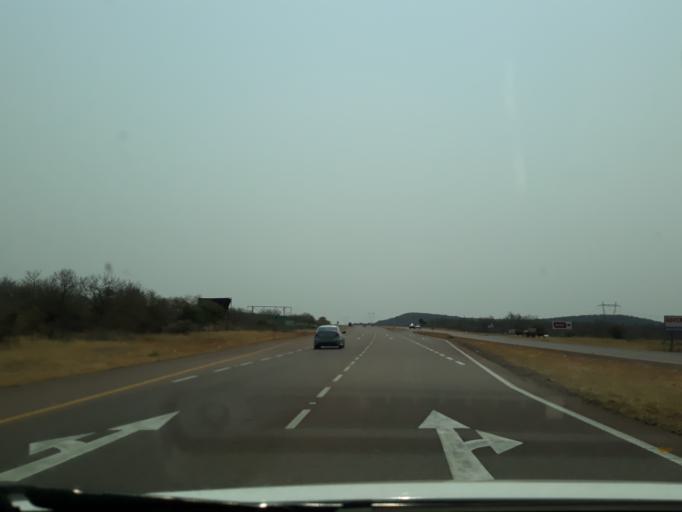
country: BW
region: Kgatleng
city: Bokaa
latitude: -24.4040
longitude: 26.0551
